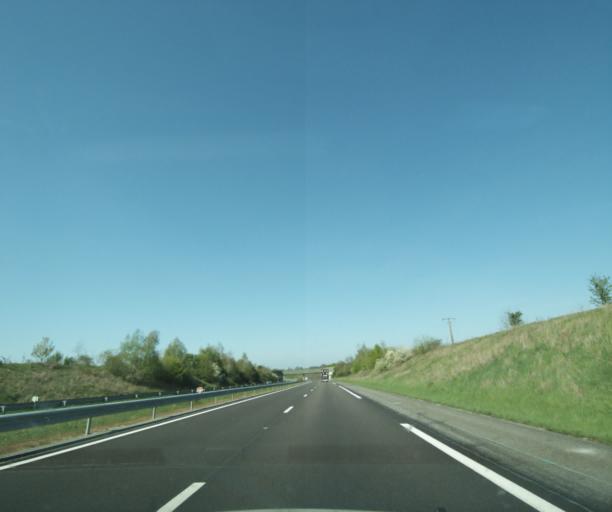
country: FR
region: Bourgogne
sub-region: Departement de la Nievre
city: Cosne-Cours-sur-Loire
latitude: 47.4713
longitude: 2.9459
